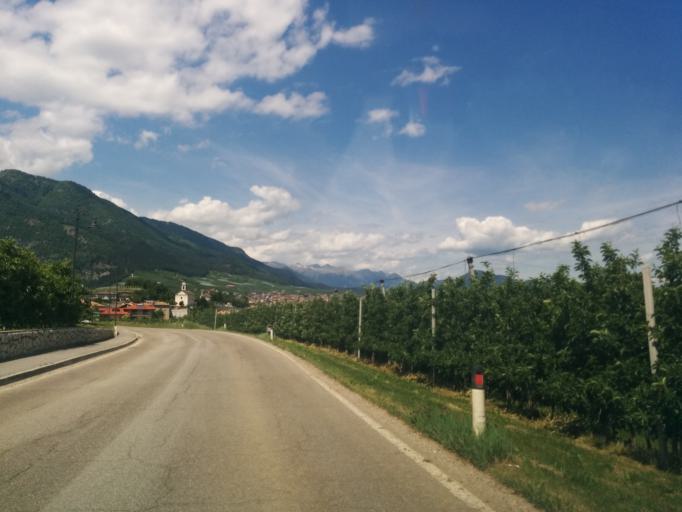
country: IT
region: Trentino-Alto Adige
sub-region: Provincia di Trento
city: Terres
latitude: 46.3052
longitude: 11.0264
